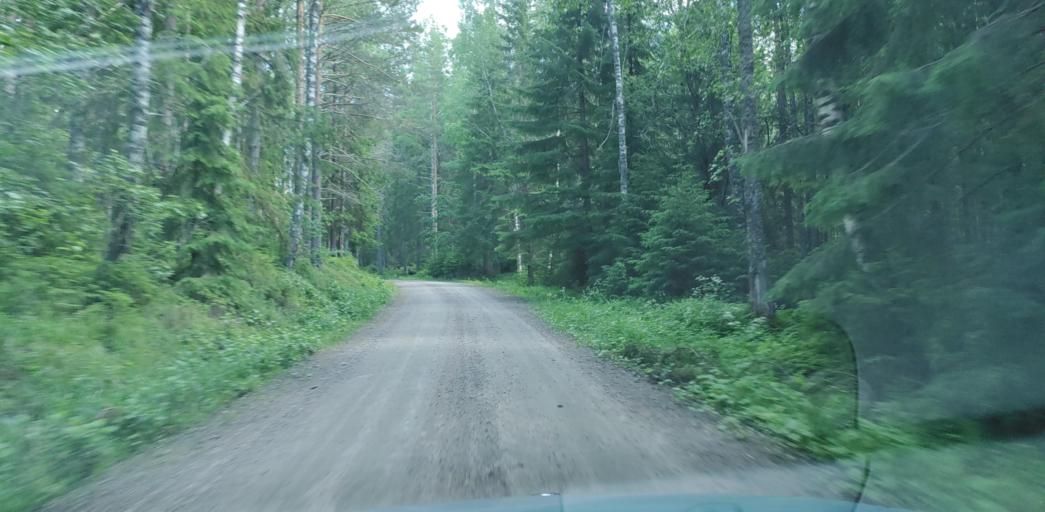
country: SE
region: Vaermland
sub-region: Hagfors Kommun
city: Ekshaerad
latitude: 60.0620
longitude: 13.3024
